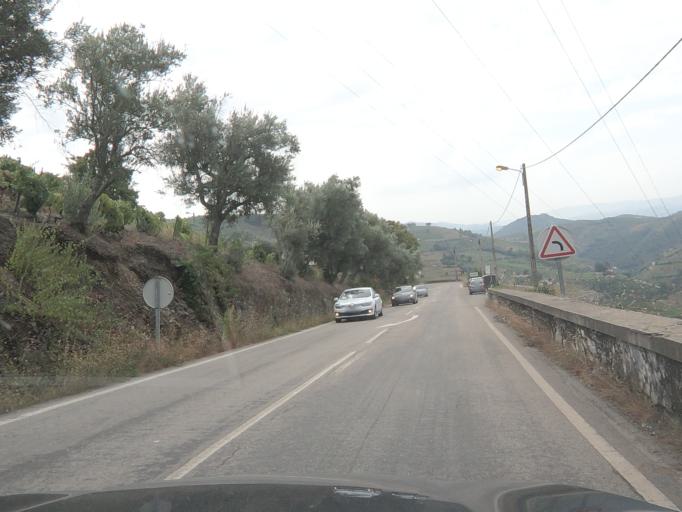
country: PT
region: Vila Real
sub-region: Santa Marta de Penaguiao
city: Santa Marta de Penaguiao
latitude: 41.2408
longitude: -7.7674
